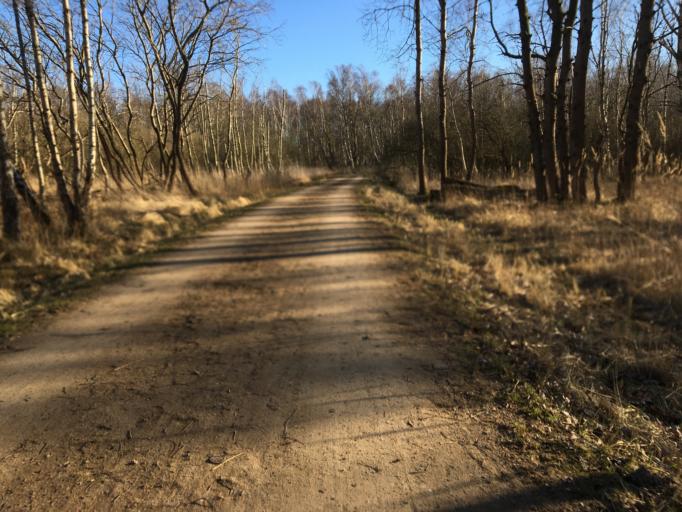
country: DK
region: Capital Region
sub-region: Tarnby Kommune
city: Tarnby
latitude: 55.5894
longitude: 12.5570
